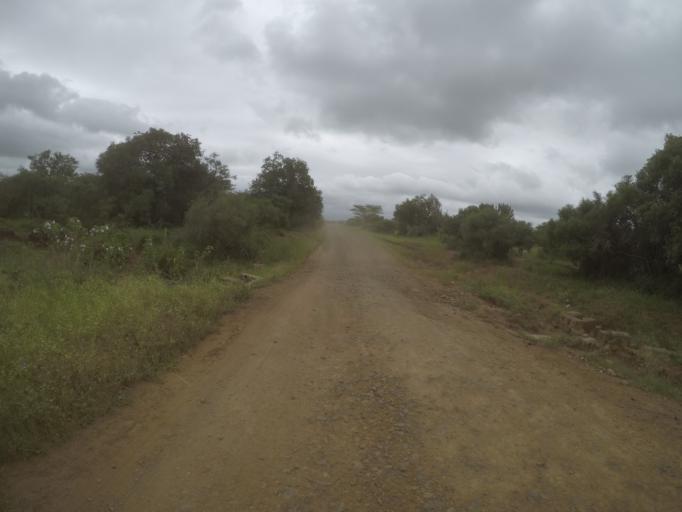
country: ZA
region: KwaZulu-Natal
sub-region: uThungulu District Municipality
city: Empangeni
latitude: -28.6104
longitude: 31.8633
